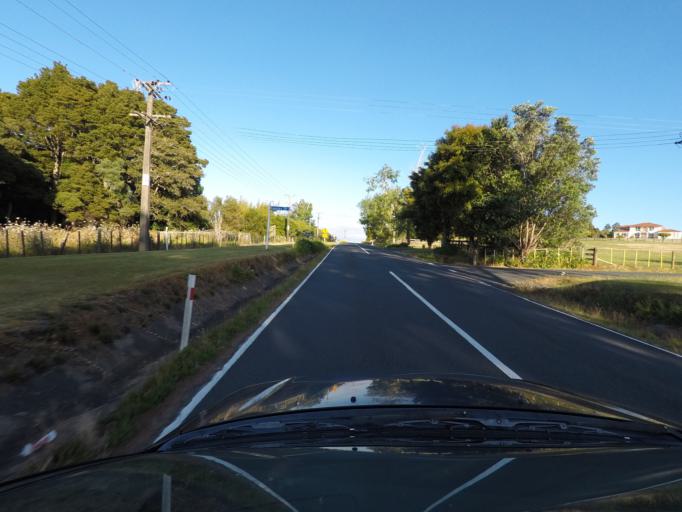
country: NZ
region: Northland
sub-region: Whangarei
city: Whangarei
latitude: -35.6591
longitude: 174.3144
